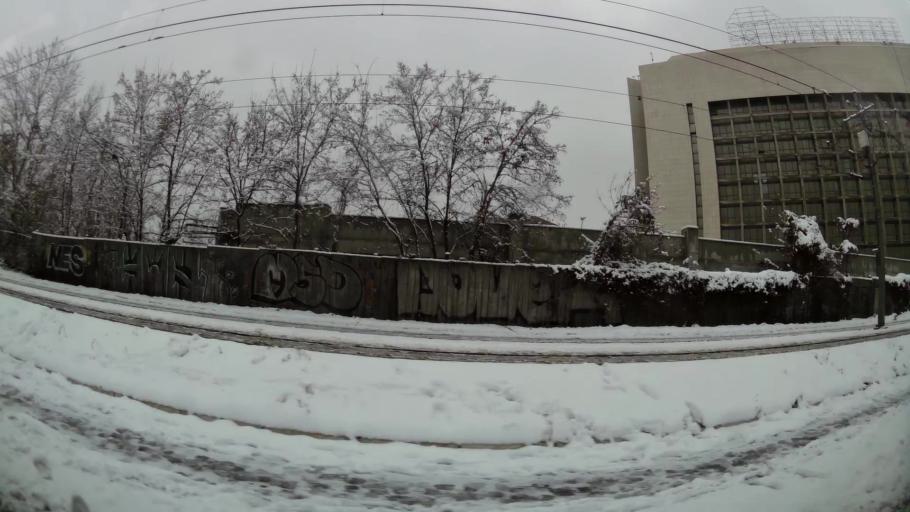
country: RS
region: Central Serbia
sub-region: Belgrade
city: Novi Beograd
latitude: 44.8124
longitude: 20.4382
